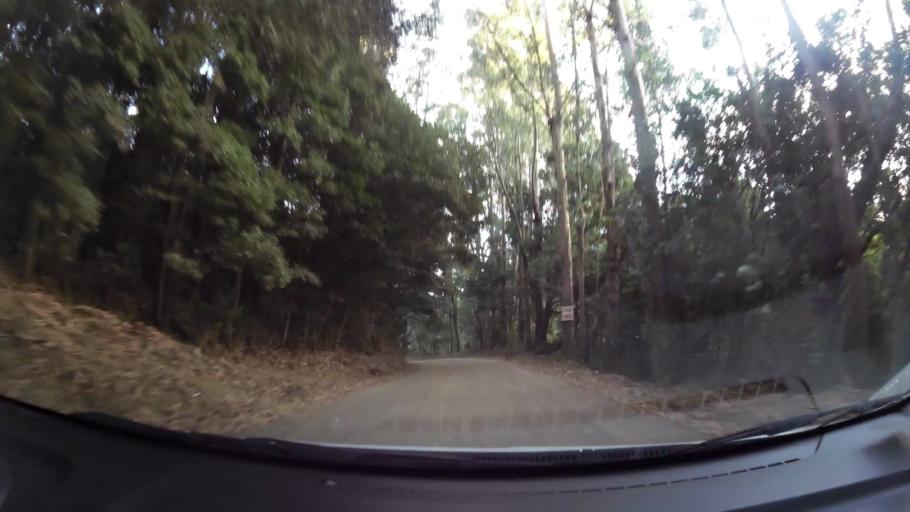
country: CL
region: Biobio
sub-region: Provincia de Concepcion
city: Concepcion
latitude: -36.8550
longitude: -73.0870
